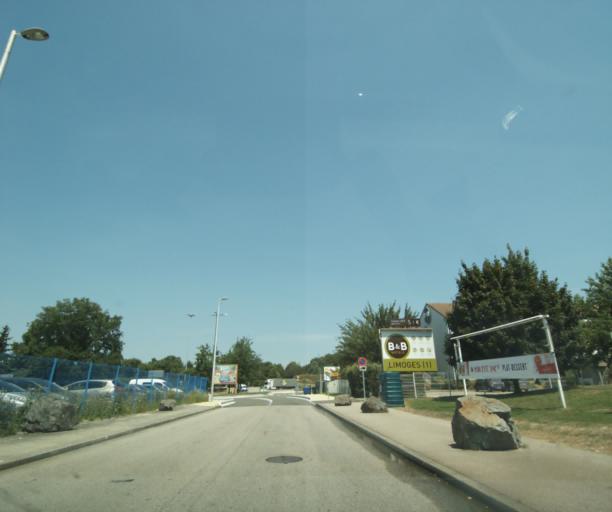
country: FR
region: Limousin
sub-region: Departement de la Haute-Vienne
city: Rilhac-Rancon
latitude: 45.8891
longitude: 1.2908
